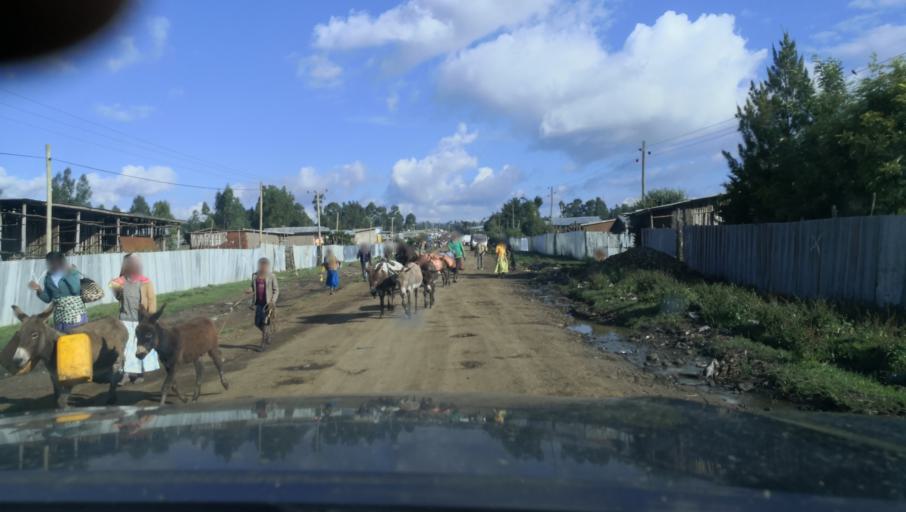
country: ET
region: Oromiya
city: Tulu Bolo
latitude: 8.4719
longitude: 38.2489
